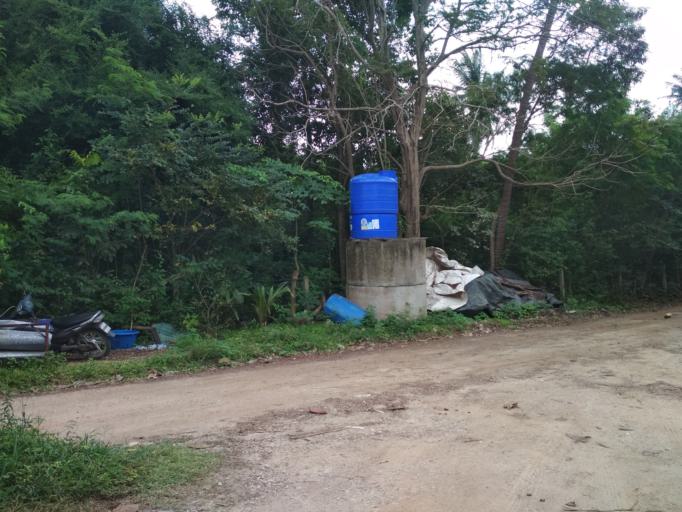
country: TH
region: Surat Thani
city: Ko Samui
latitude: 9.5714
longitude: 99.9158
